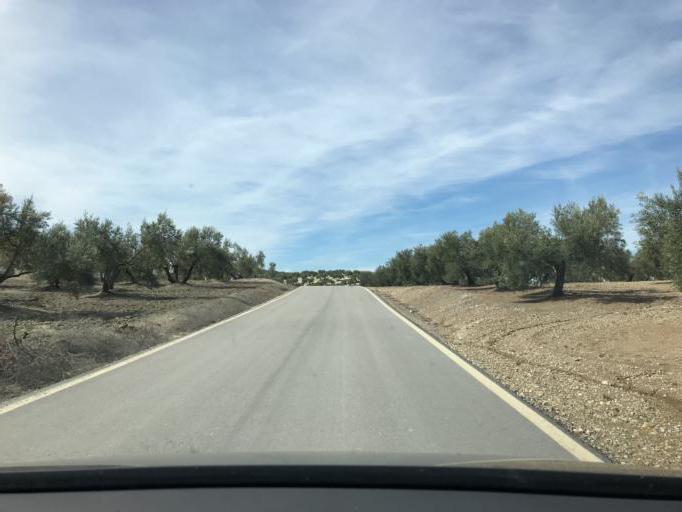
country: ES
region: Andalusia
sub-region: Provincia de Jaen
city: Higuera de Calatrava
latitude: 37.7921
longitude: -4.1097
